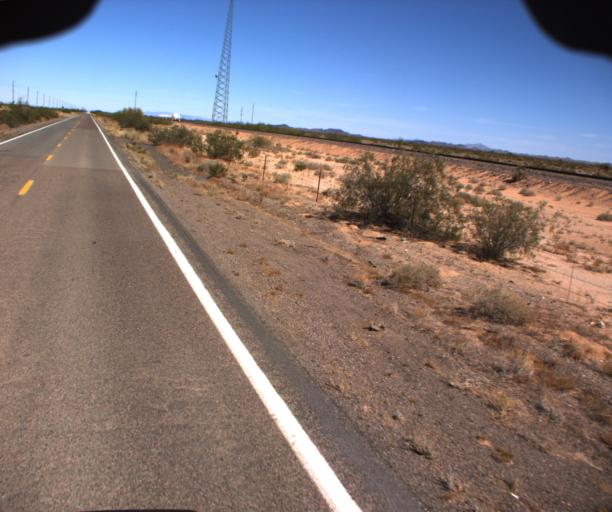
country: US
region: Arizona
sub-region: La Paz County
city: Salome
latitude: 33.8362
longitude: -113.8836
